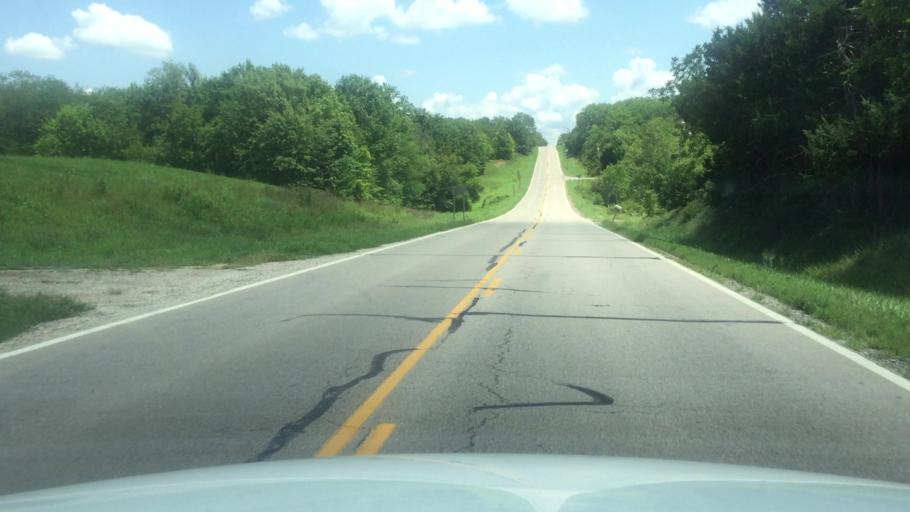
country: US
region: Kansas
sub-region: Brown County
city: Horton
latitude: 39.6673
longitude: -95.5404
